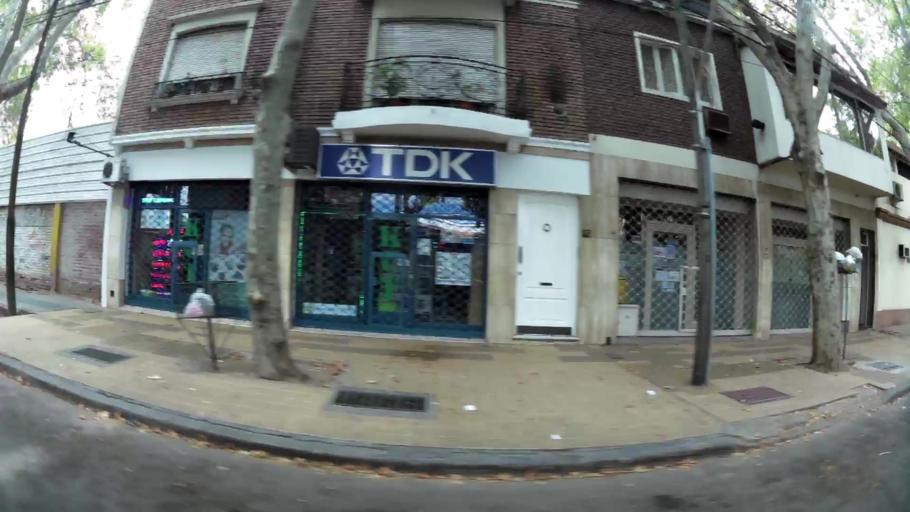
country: AR
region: Mendoza
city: Mendoza
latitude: -32.8832
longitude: -68.8401
